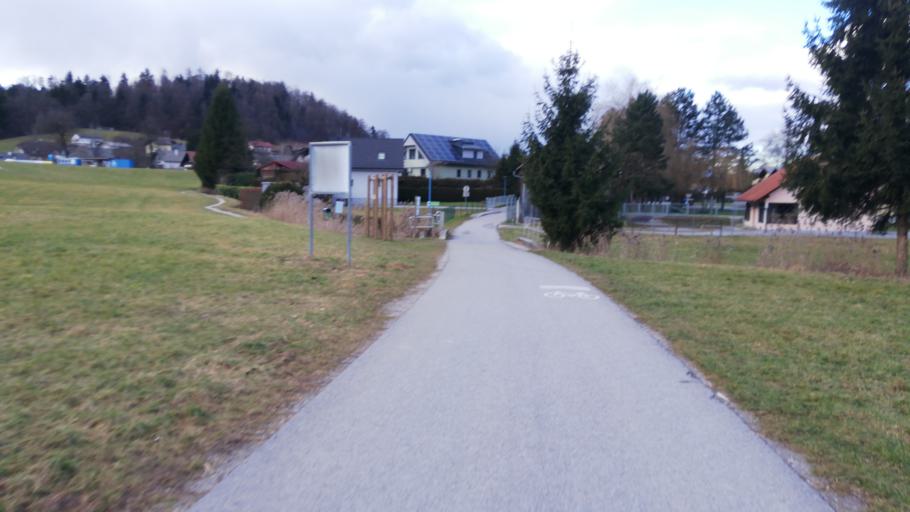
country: SI
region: Medvode
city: Medvode
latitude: 46.1289
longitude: 14.4150
